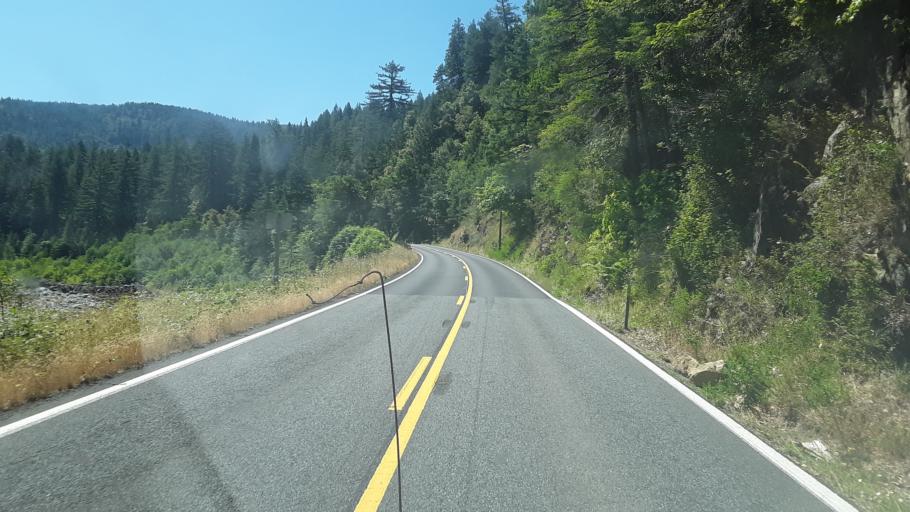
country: US
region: California
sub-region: Del Norte County
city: Bertsch-Oceanview
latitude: 41.8361
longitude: -124.0364
